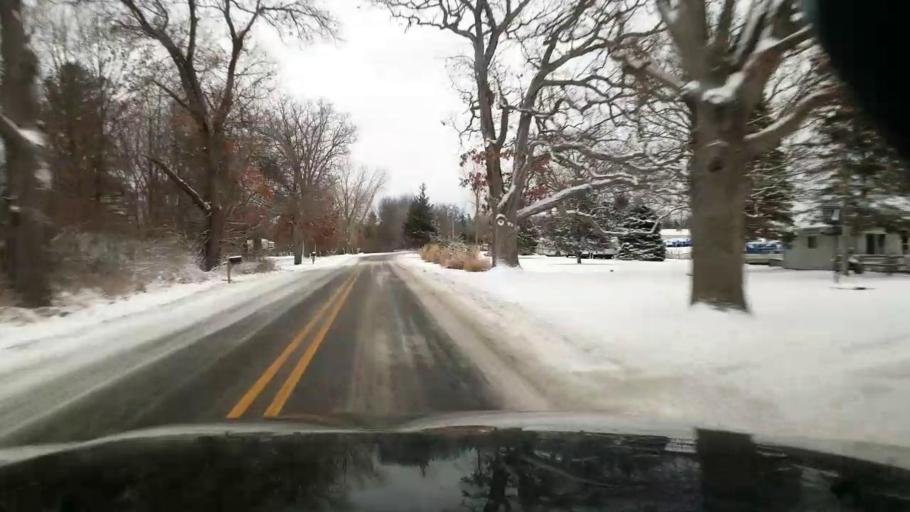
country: US
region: Michigan
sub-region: Jackson County
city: Vandercook Lake
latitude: 42.0974
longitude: -84.4791
